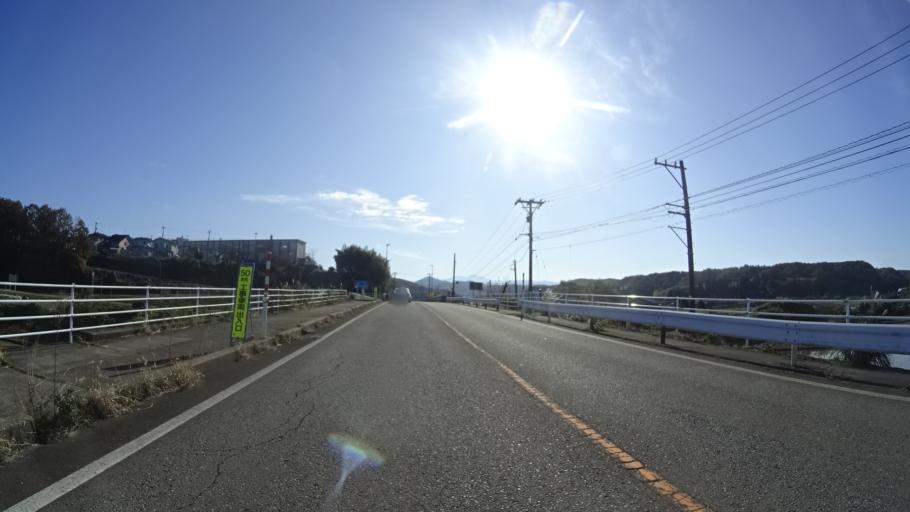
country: JP
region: Ishikawa
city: Komatsu
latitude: 36.3982
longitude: 136.5160
